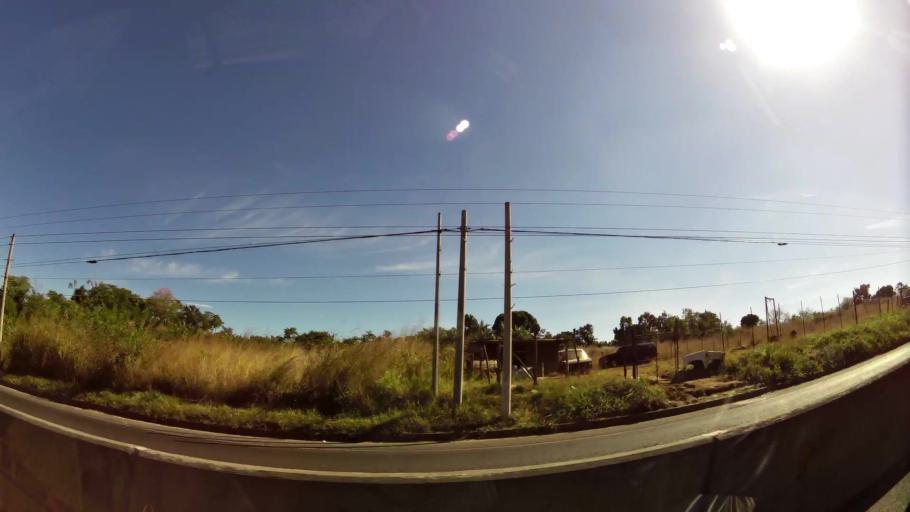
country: SV
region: Santa Ana
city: Coatepeque
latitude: 13.9270
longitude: -89.5209
